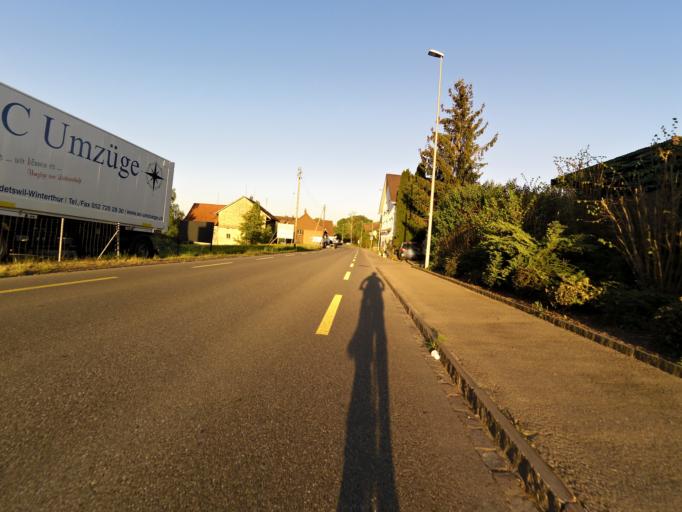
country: CH
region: Zurich
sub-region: Bezirk Winterthur
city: Sulz
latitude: 47.5398
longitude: 8.8196
